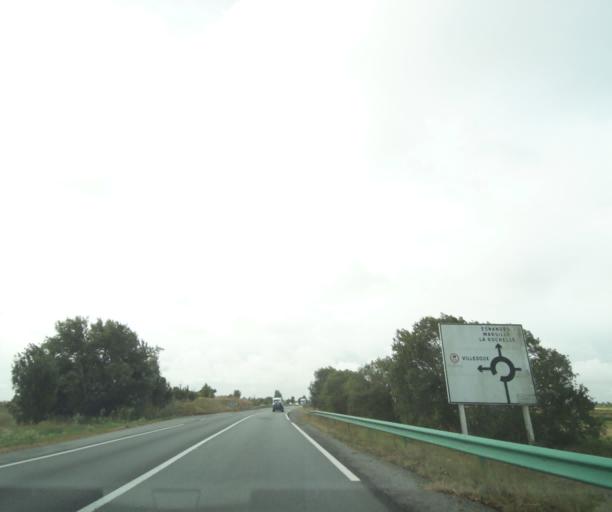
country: FR
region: Poitou-Charentes
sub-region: Departement de la Charente-Maritime
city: Andilly
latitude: 46.2551
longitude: -1.0663
